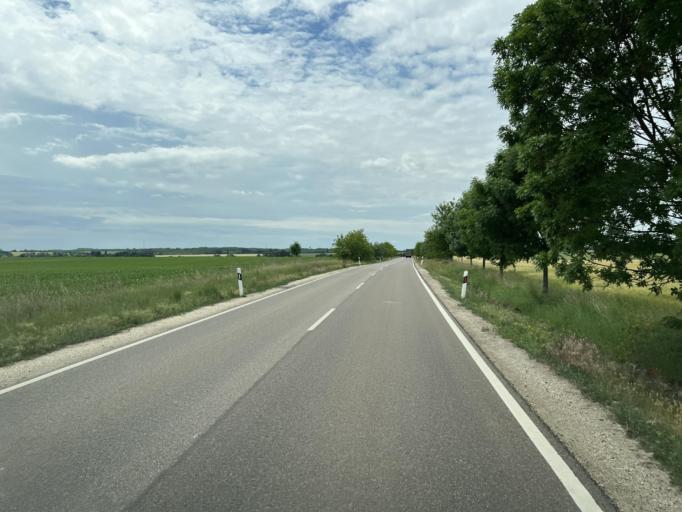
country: HU
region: Pest
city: Koka
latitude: 47.5126
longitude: 19.5977
